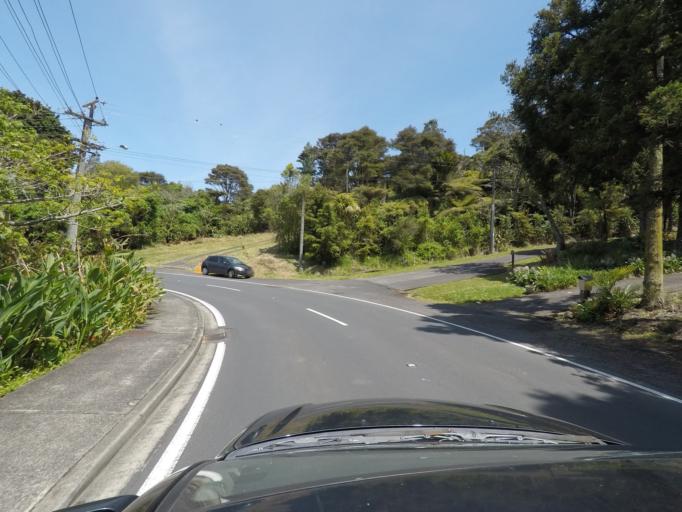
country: NZ
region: Auckland
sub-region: Auckland
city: Titirangi
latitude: -36.9653
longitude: 174.6383
